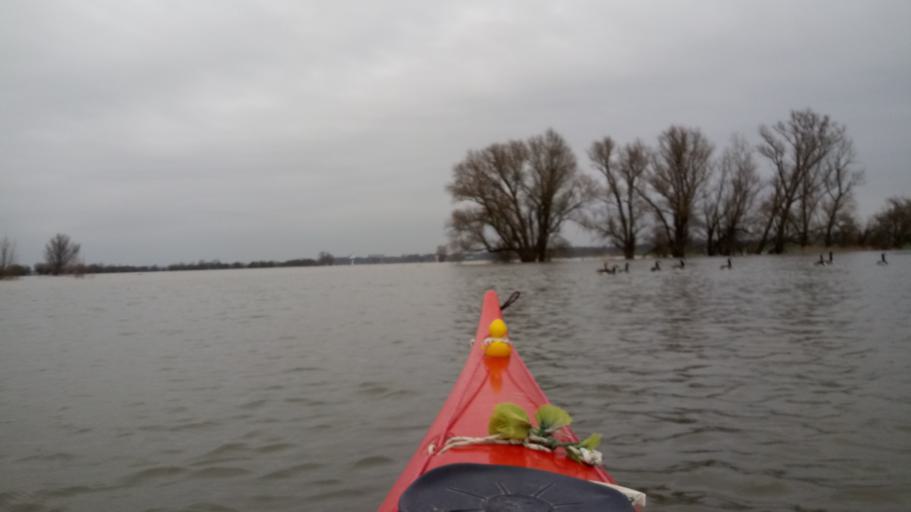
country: NL
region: Gelderland
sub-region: Gemeente Zutphen
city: Zutphen
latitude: 52.1644
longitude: 6.1899
